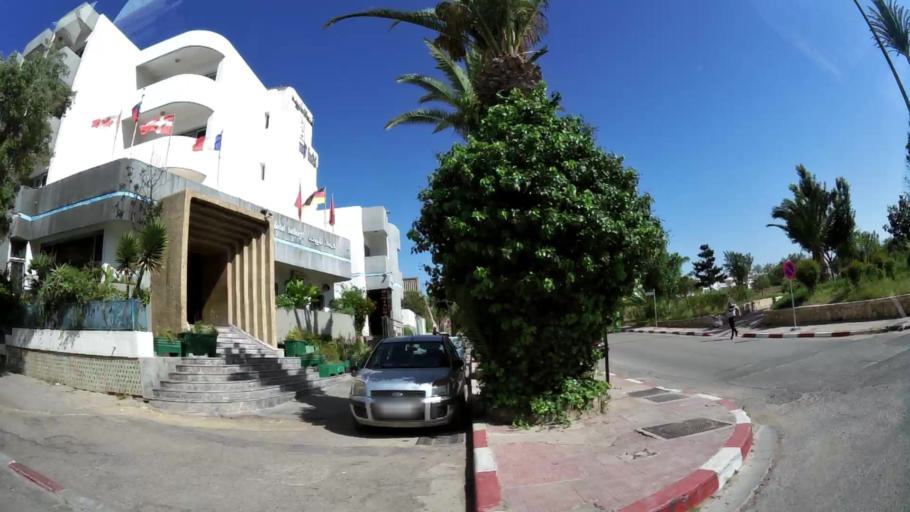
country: MA
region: Souss-Massa-Draa
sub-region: Agadir-Ida-ou-Tnan
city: Agadir
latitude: 30.4225
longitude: -9.5980
